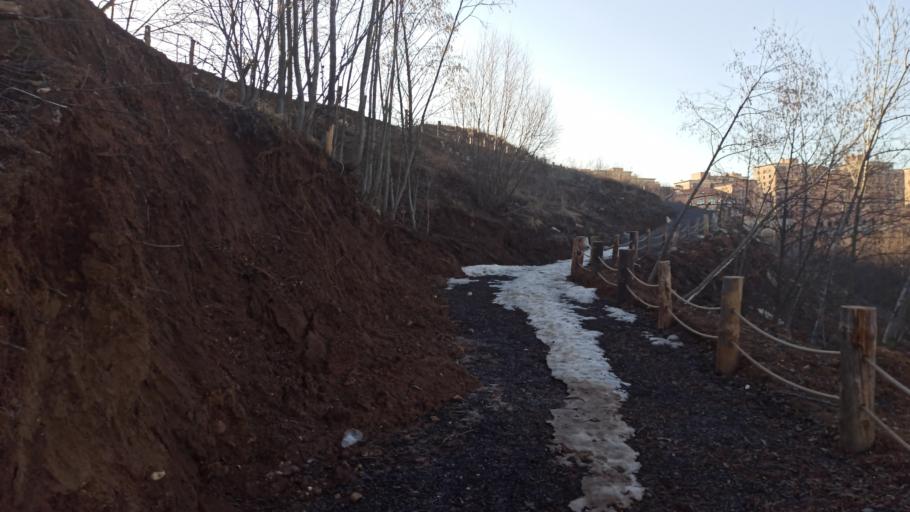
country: RU
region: Moskovskaya
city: Novopodrezkovo
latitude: 55.9395
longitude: 37.3243
